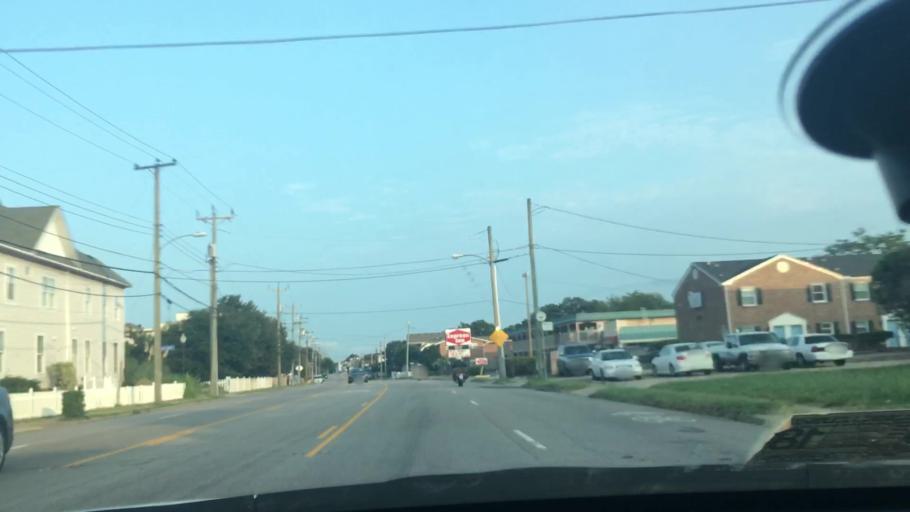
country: US
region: Virginia
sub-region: City of Norfolk
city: Norfolk
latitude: 36.9462
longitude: -76.2391
